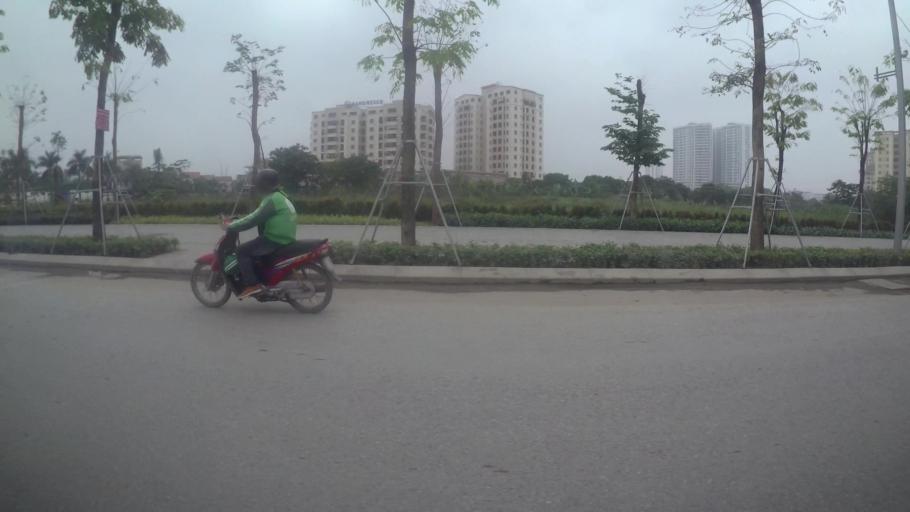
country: VN
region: Ha Noi
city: Tay Ho
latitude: 21.0644
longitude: 105.7844
